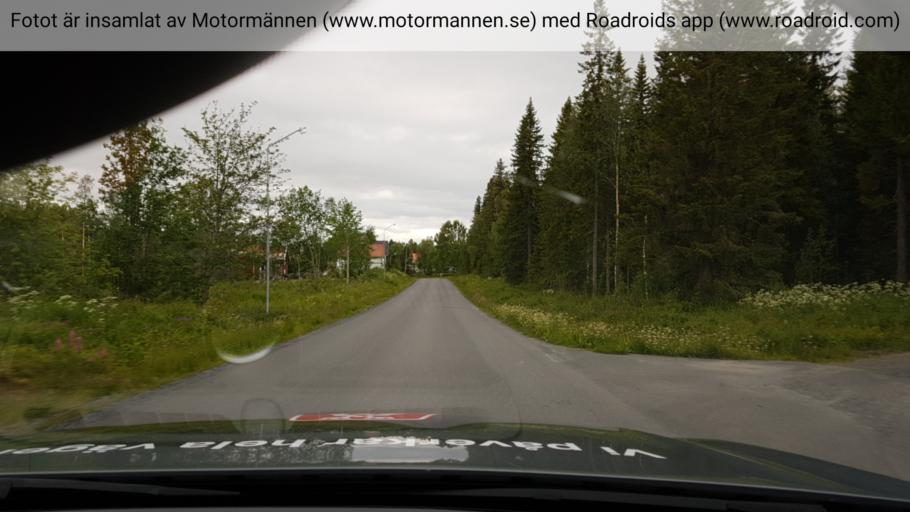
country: SE
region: Jaemtland
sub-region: OEstersunds Kommun
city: Lit
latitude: 63.5642
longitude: 14.9361
